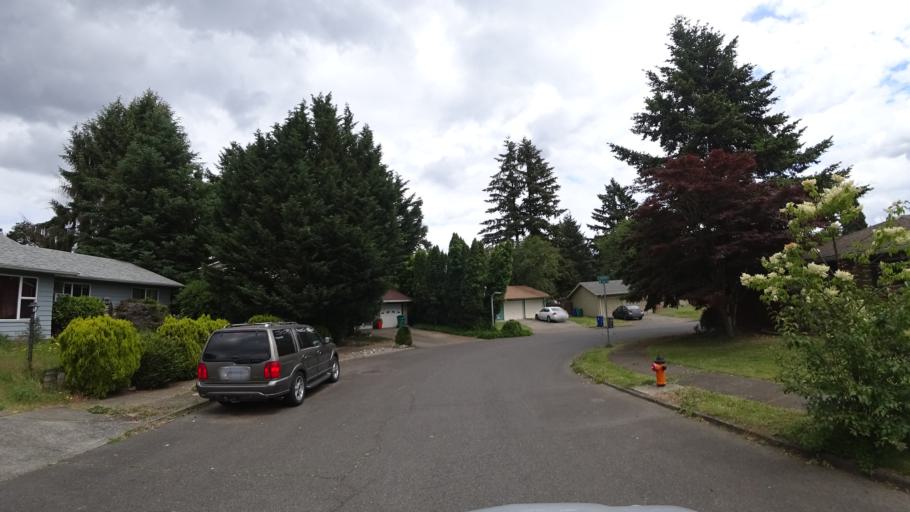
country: US
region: Oregon
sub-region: Multnomah County
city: Lents
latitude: 45.5016
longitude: -122.5154
